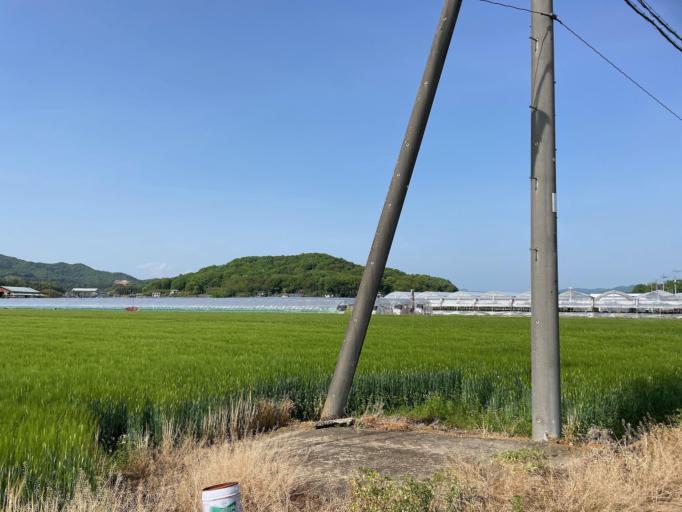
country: JP
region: Gunma
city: Tatebayashi
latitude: 36.3052
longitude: 139.5279
